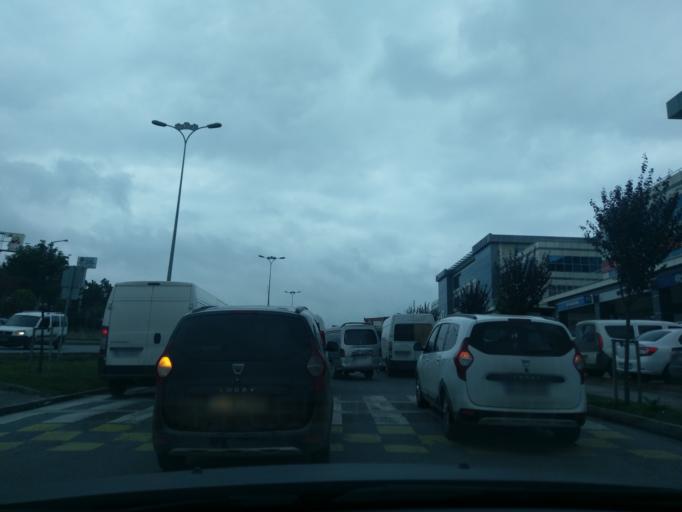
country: TR
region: Istanbul
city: Basaksehir
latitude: 41.0760
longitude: 28.7989
